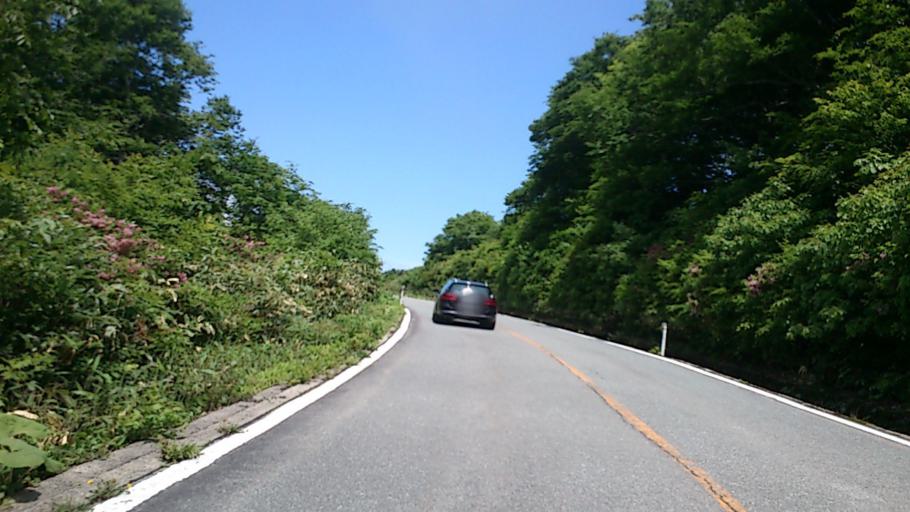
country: JP
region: Yamagata
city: Yamagata-shi
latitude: 38.1196
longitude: 140.4176
